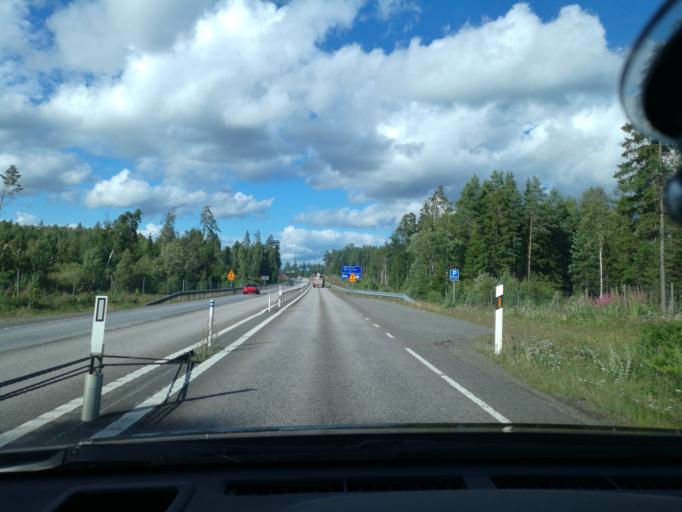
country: SE
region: Kronoberg
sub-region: Vaxjo Kommun
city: Braas
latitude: 57.0127
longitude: 15.0498
